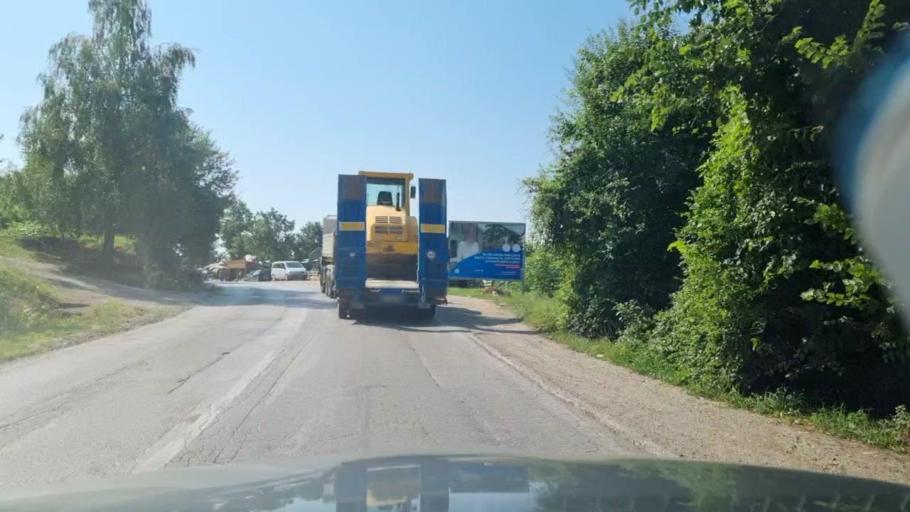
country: BA
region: Federation of Bosnia and Herzegovina
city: Gradacac
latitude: 44.8579
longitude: 18.4301
